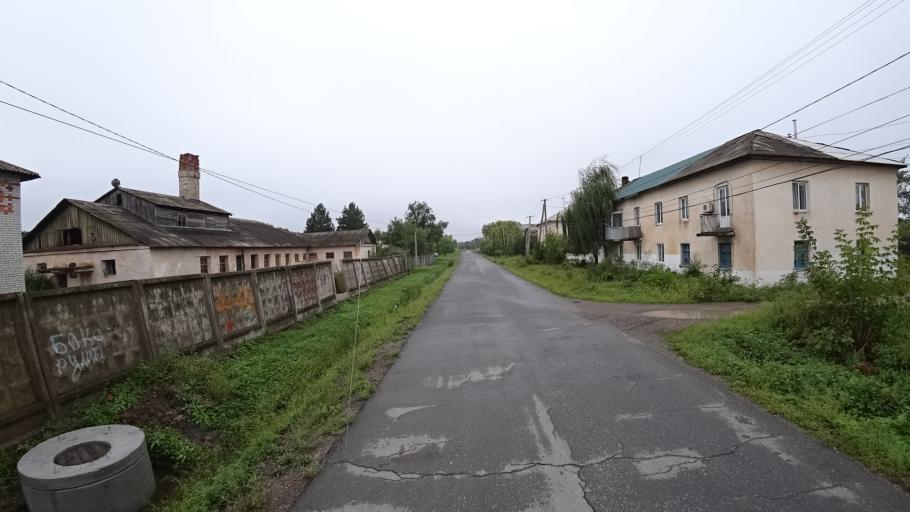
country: RU
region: Primorskiy
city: Monastyrishche
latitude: 44.1981
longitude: 132.4304
